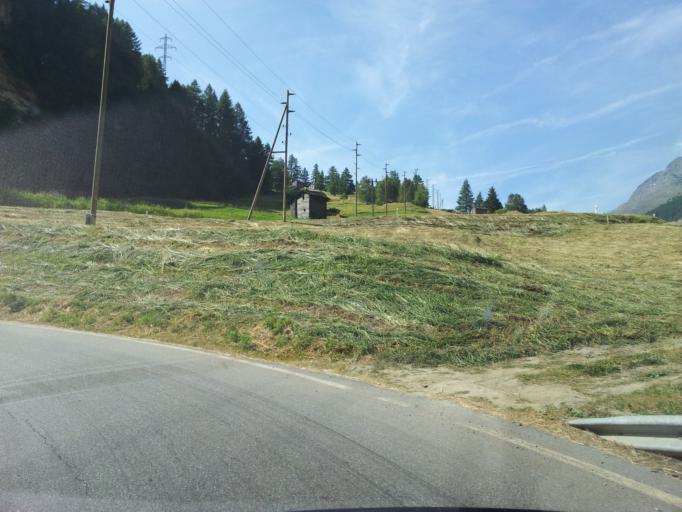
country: CH
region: Valais
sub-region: Visp District
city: Sankt Niklaus
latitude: 46.1102
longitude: 7.7866
